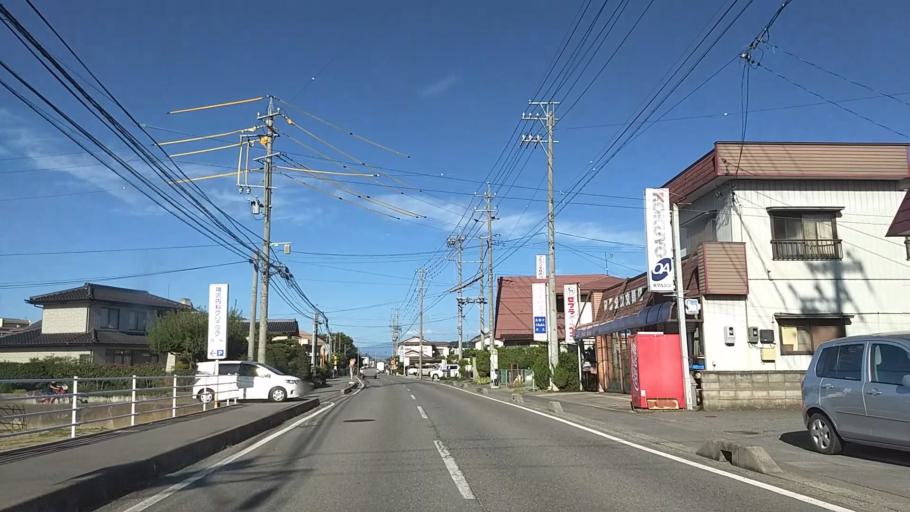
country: JP
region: Nagano
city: Nagano-shi
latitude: 36.5429
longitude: 138.1324
